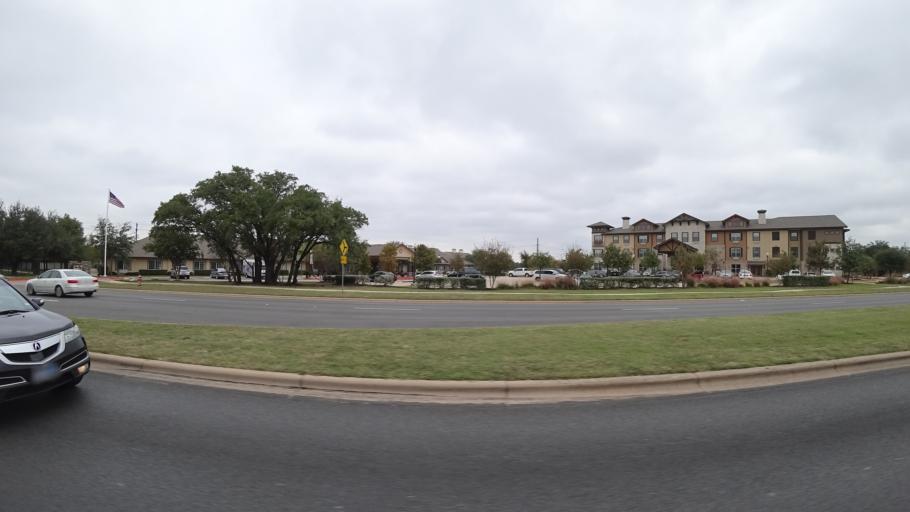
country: US
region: Texas
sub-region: Williamson County
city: Cedar Park
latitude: 30.4798
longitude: -97.8232
